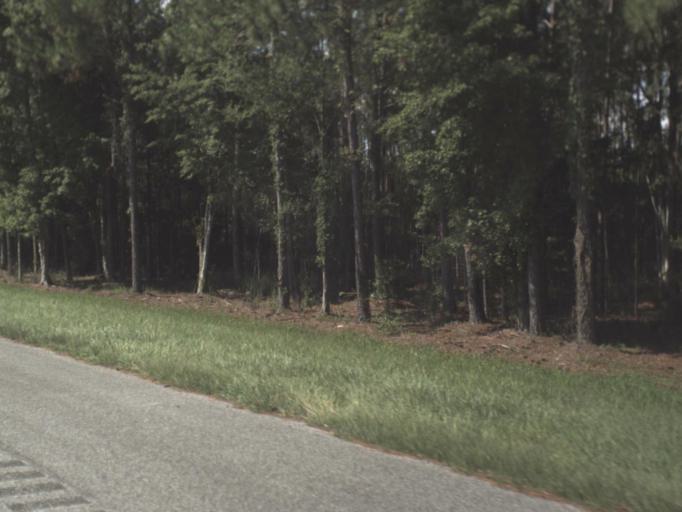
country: US
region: Florida
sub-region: Saint Johns County
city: Fruit Cove
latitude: 30.0355
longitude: -81.4918
